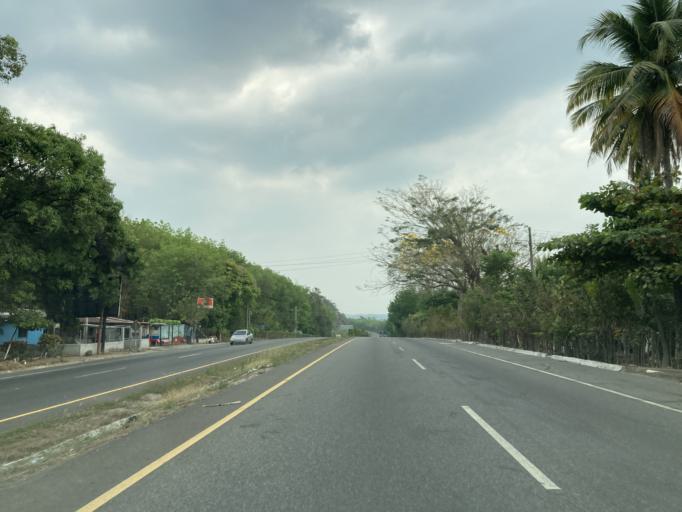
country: GT
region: Suchitepeque
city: Santa Barbara
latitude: 14.3937
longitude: -91.2348
